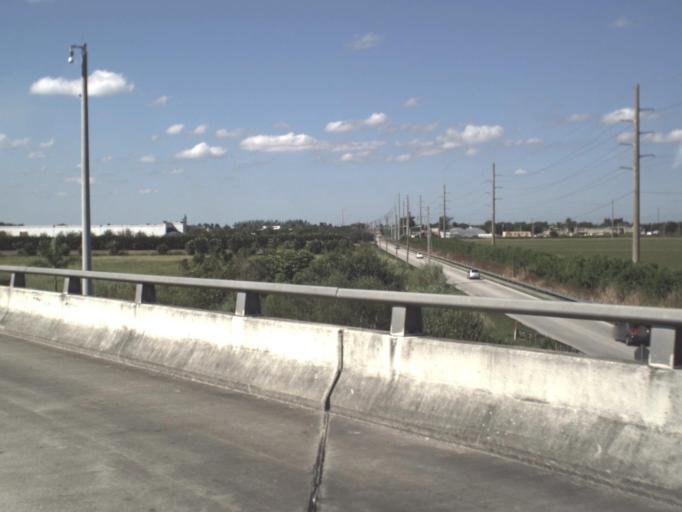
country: US
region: Florida
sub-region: Miami-Dade County
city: Homestead
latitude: 25.4624
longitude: -80.4626
